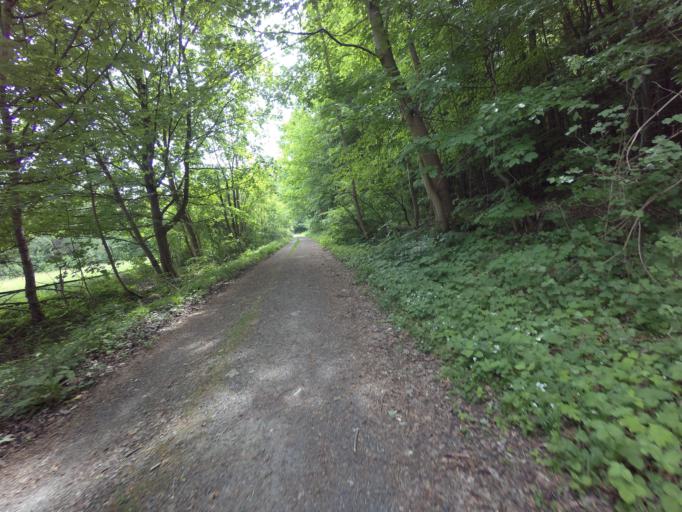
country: DE
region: Lower Saxony
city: Erkerode
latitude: 52.2058
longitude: 10.7371
